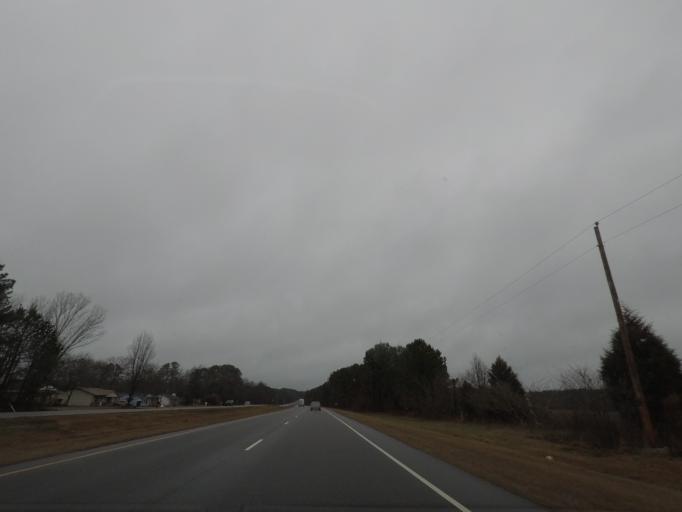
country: US
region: North Carolina
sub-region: Lee County
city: Broadway
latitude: 35.3204
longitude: -79.0909
